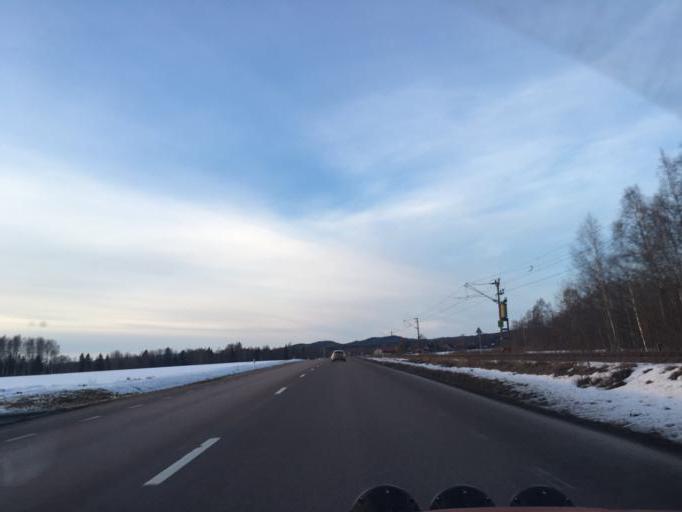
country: SE
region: Dalarna
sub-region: Gagnefs Kommun
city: Djuras
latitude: 60.5700
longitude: 15.1256
